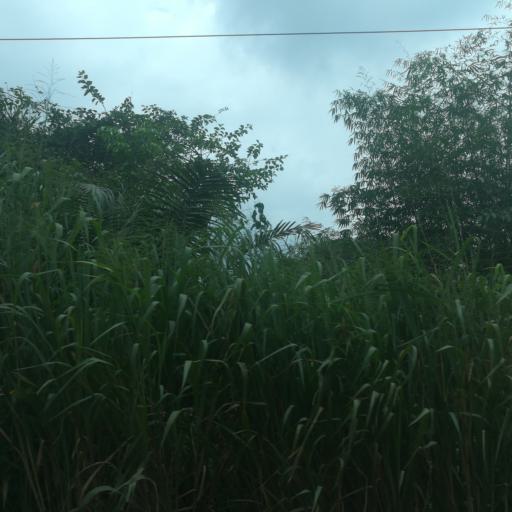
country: NG
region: Lagos
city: Ejirin
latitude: 6.6611
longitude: 3.8150
